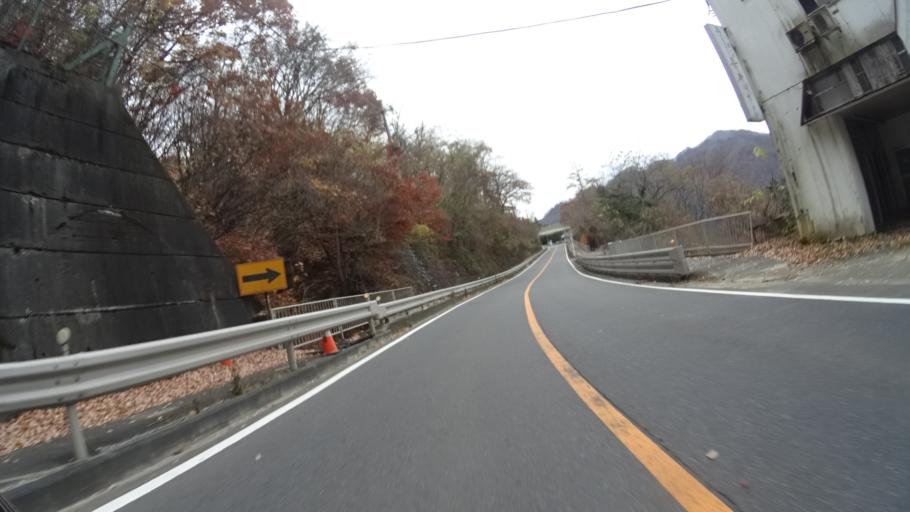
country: JP
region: Gunma
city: Nakanojomachi
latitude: 36.7289
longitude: 138.8943
